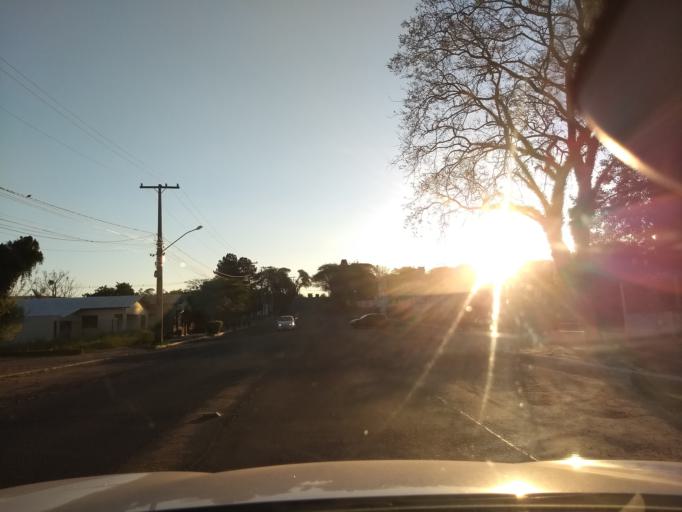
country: BR
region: Rio Grande do Sul
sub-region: Santa Cruz Do Sul
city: Santa Cruz do Sul
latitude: -29.7153
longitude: -52.5076
